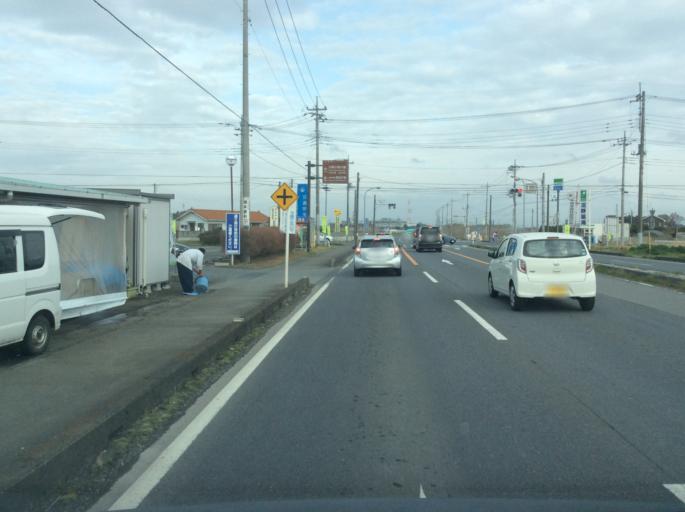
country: JP
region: Ibaraki
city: Naka
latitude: 36.1313
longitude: 140.1561
